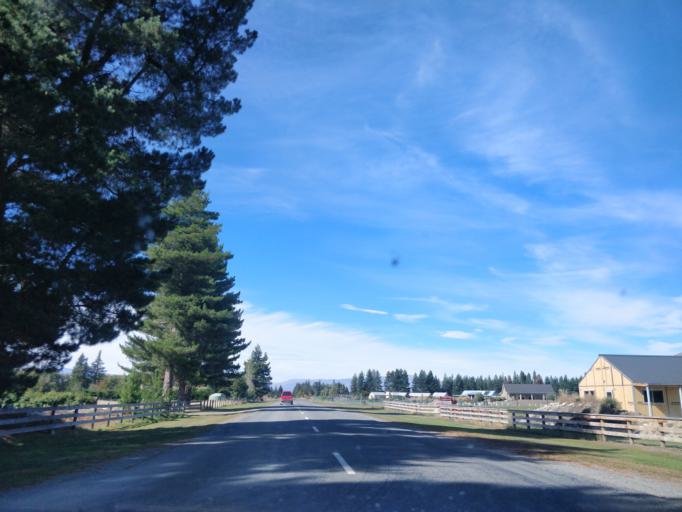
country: NZ
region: Otago
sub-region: Queenstown-Lakes District
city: Wanaka
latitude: -44.2406
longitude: 170.0838
